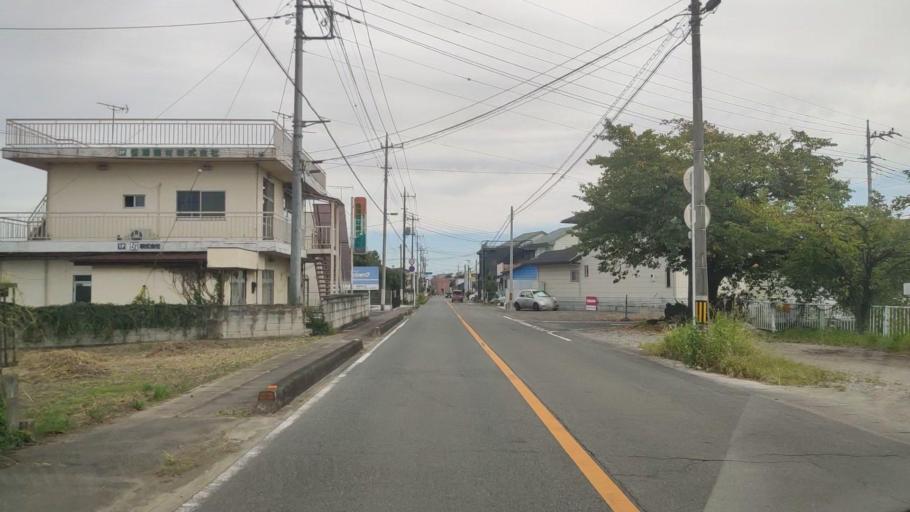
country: JP
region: Gunma
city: Takasaki
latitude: 36.3604
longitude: 138.9850
